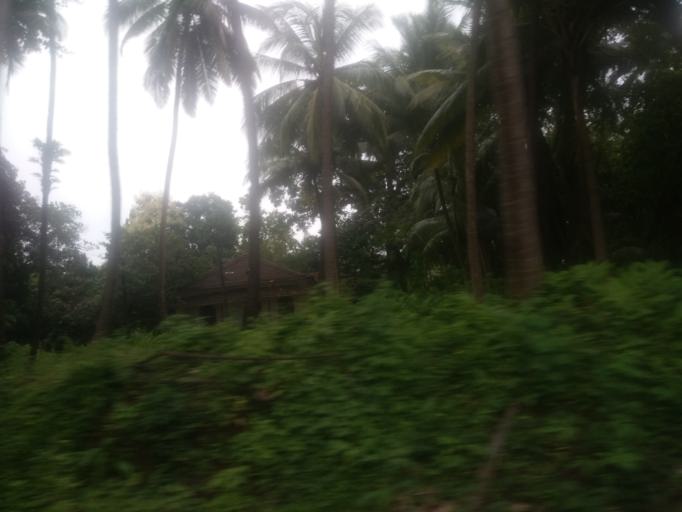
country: IN
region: Goa
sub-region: South Goa
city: Varca
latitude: 15.2152
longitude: 73.9501
